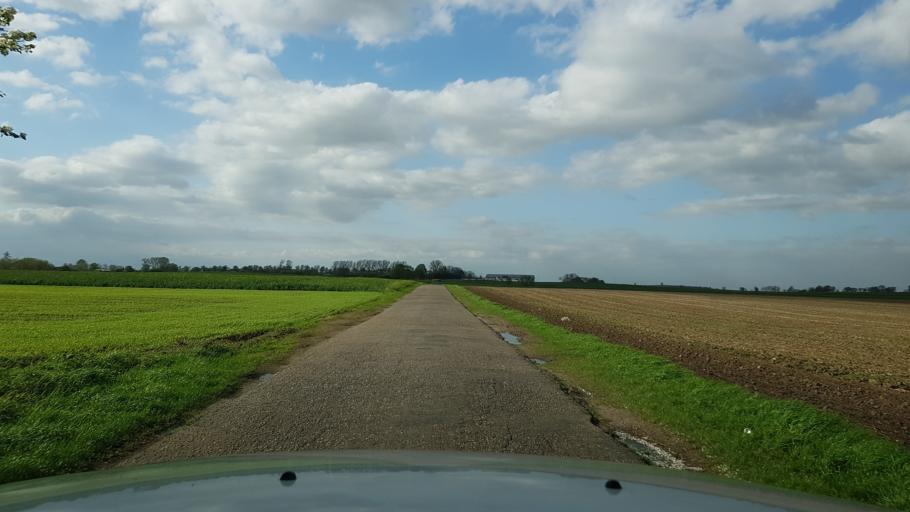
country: PL
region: West Pomeranian Voivodeship
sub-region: Powiat pyrzycki
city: Przelewice
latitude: 53.0642
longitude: 15.1053
